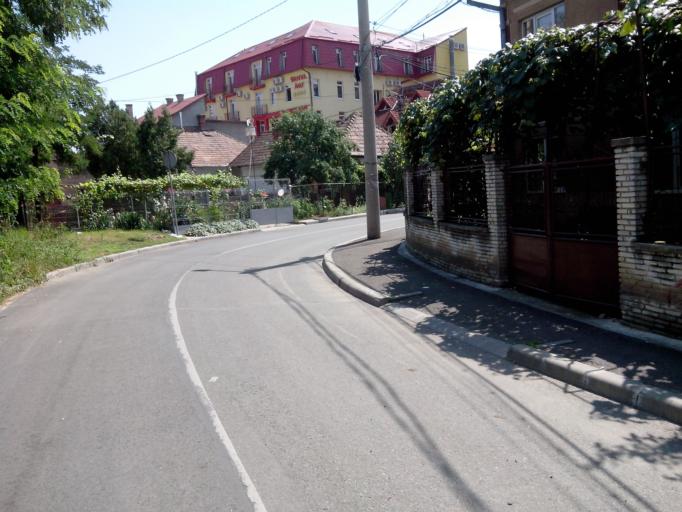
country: RO
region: Cluj
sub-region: Municipiul Cluj-Napoca
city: Cluj-Napoca
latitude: 46.7817
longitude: 23.5786
